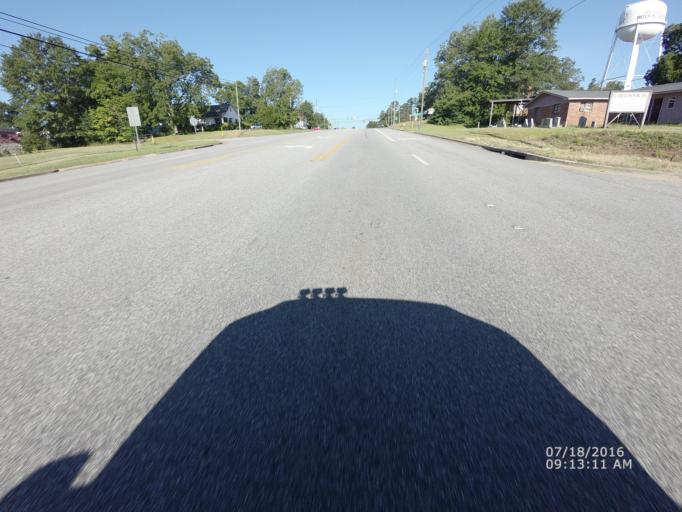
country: US
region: Alabama
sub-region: Chambers County
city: Huguley
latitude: 32.8466
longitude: -85.2308
